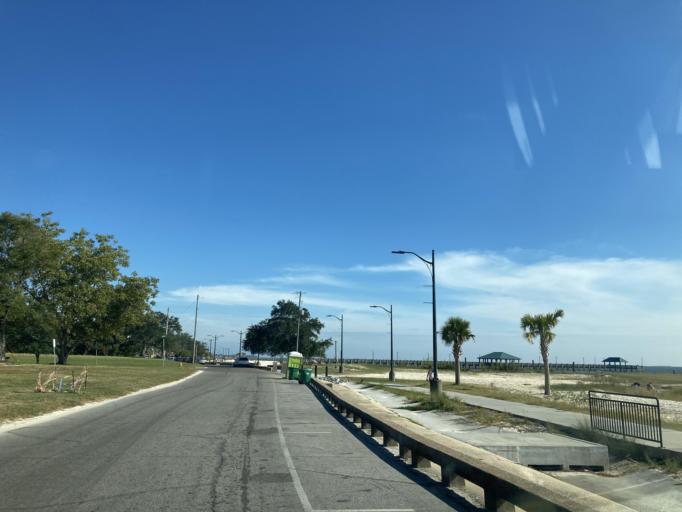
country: US
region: Mississippi
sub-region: Jackson County
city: Ocean Springs
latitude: 30.4065
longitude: -88.8311
